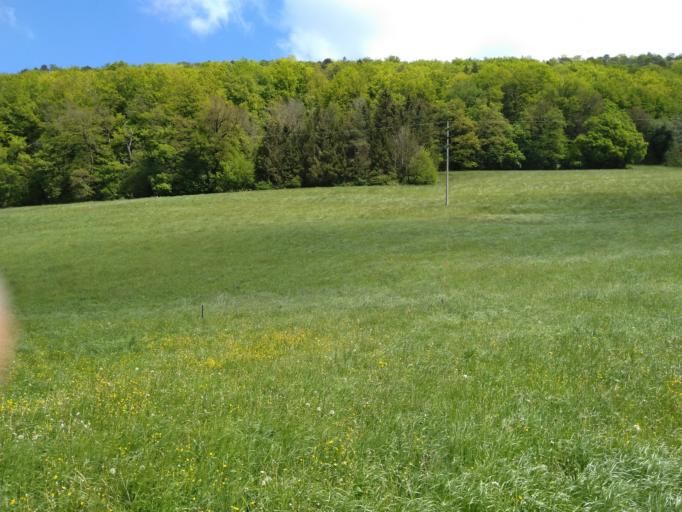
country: CH
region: Basel-Landschaft
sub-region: Bezirk Laufen
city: Wahlen
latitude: 47.3837
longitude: 7.4870
